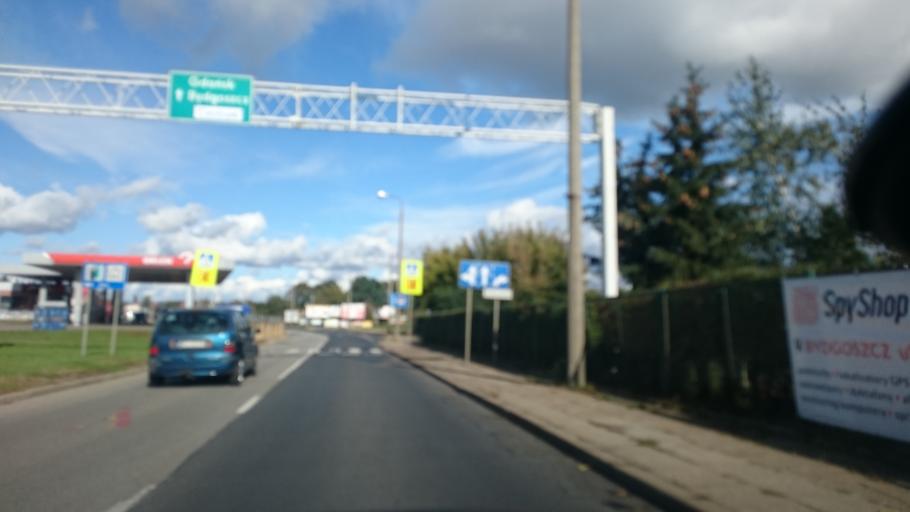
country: PL
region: Kujawsko-Pomorskie
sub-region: Grudziadz
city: Grudziadz
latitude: 53.4629
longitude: 18.7415
